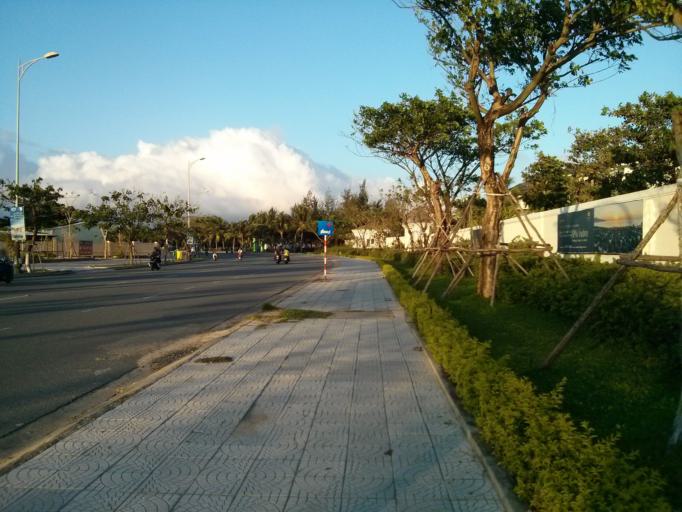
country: VN
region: Da Nang
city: Son Tra
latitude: 16.0452
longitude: 108.2490
